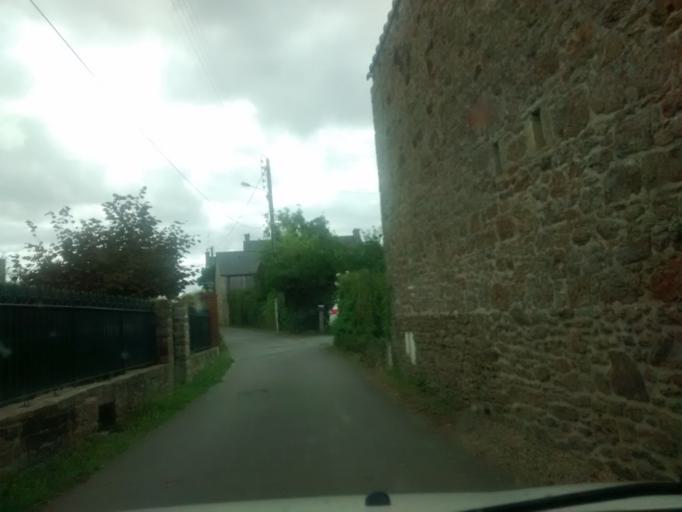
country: FR
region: Brittany
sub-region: Departement d'Ille-et-Vilaine
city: Saint-Briac-sur-Mer
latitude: 48.6229
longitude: -2.1347
